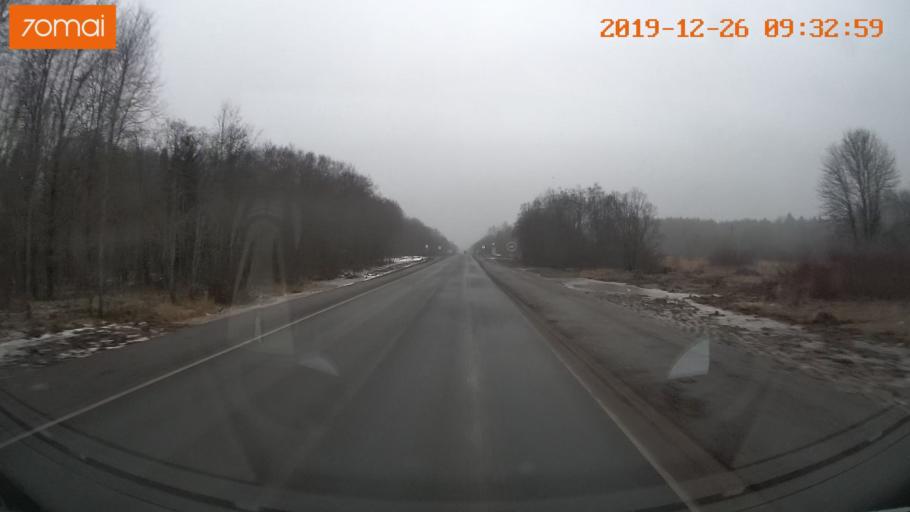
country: RU
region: Vologda
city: Gryazovets
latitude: 59.0844
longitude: 40.1079
